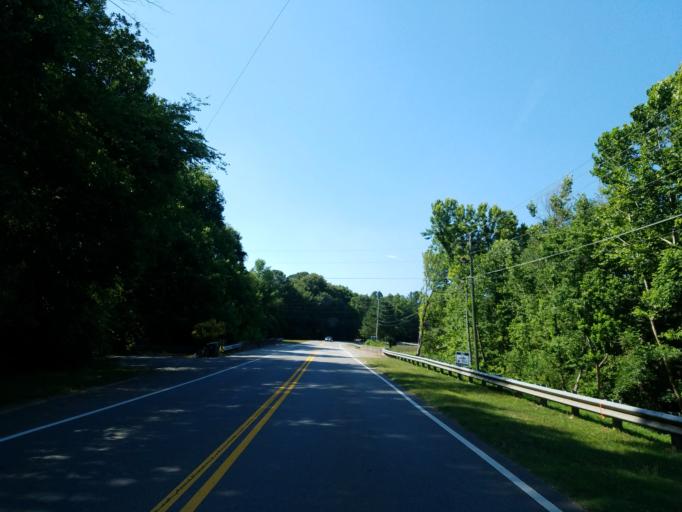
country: US
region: Georgia
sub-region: Fulton County
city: Milton
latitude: 34.1290
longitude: -84.3438
